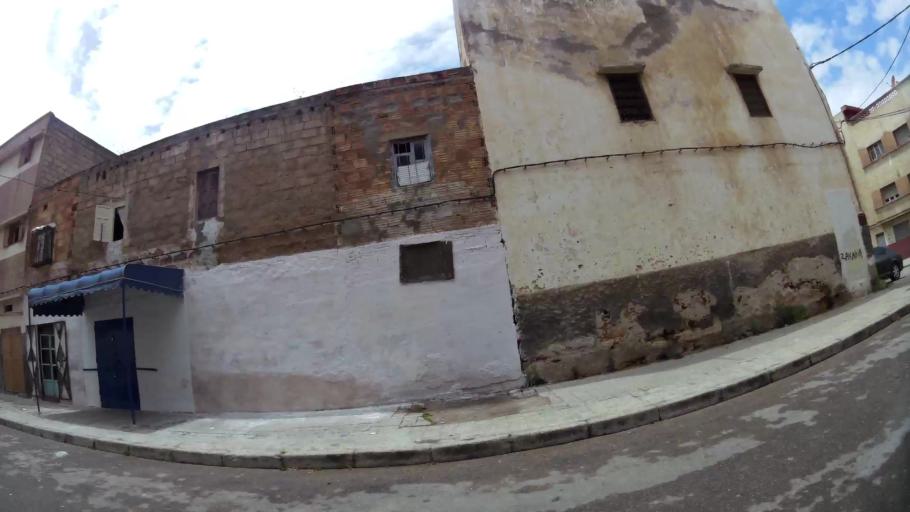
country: MA
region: Rabat-Sale-Zemmour-Zaer
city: Sale
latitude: 34.0412
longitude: -6.8119
